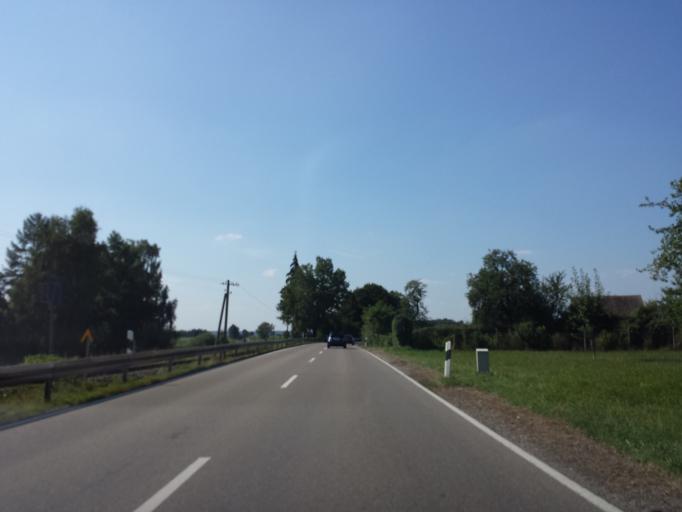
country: DE
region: Bavaria
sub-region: Swabia
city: Pfaffenhausen
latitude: 48.1196
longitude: 10.4497
